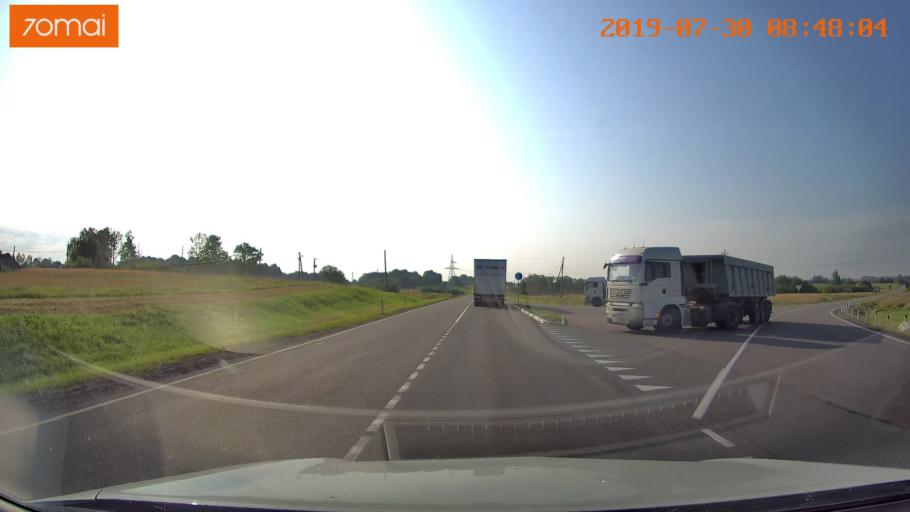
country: RU
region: Kaliningrad
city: Chernyakhovsk
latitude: 54.6198
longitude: 21.9002
